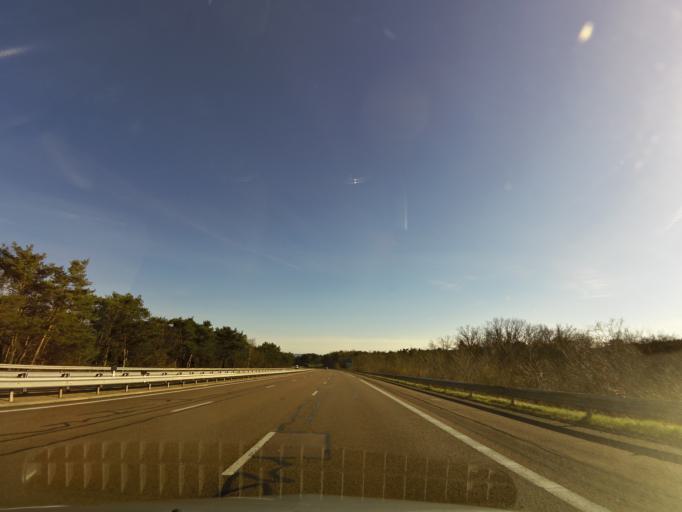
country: FR
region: Bourgogne
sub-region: Departement de l'Yonne
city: Appoigny
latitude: 47.8688
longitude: 3.4885
